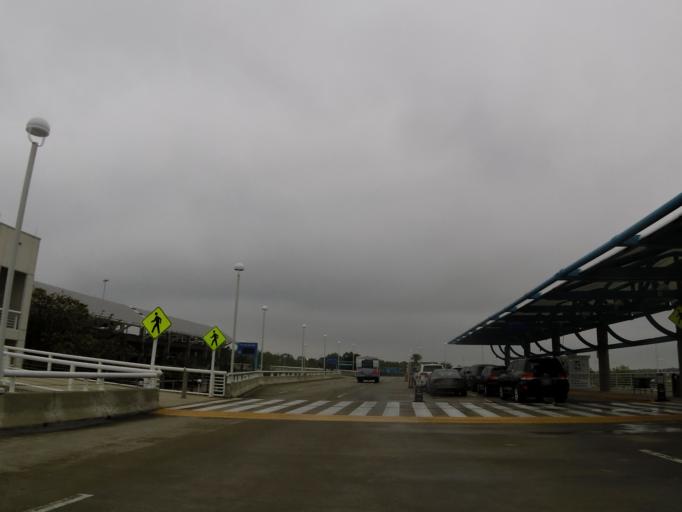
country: US
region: Florida
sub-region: Nassau County
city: Nassau Village-Ratliff
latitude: 30.4907
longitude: -81.6831
